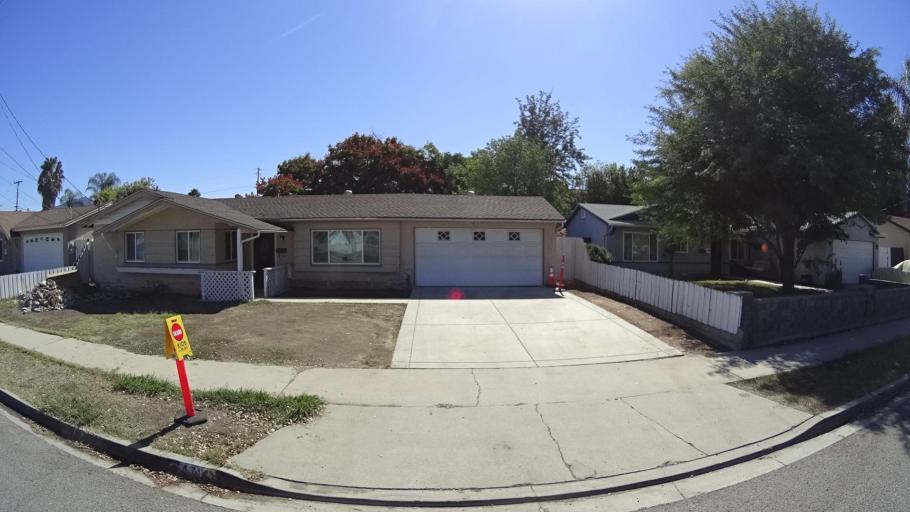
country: US
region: California
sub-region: San Diego County
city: La Presa
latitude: 32.7030
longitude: -117.0144
